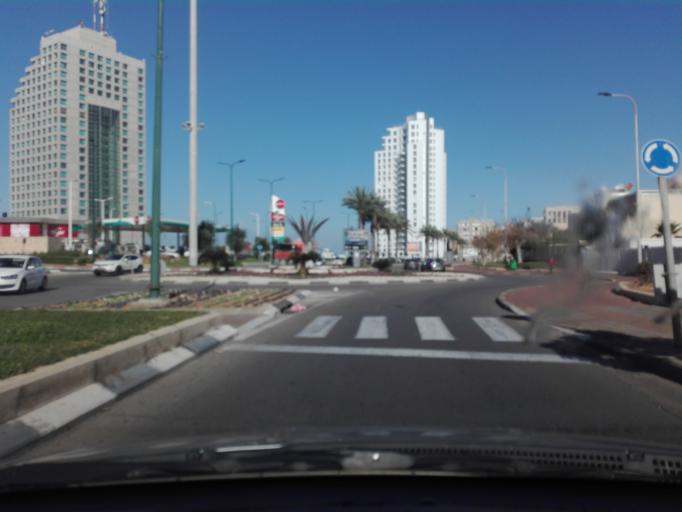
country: IL
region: Central District
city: Netanya
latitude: 32.3165
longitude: 34.8480
